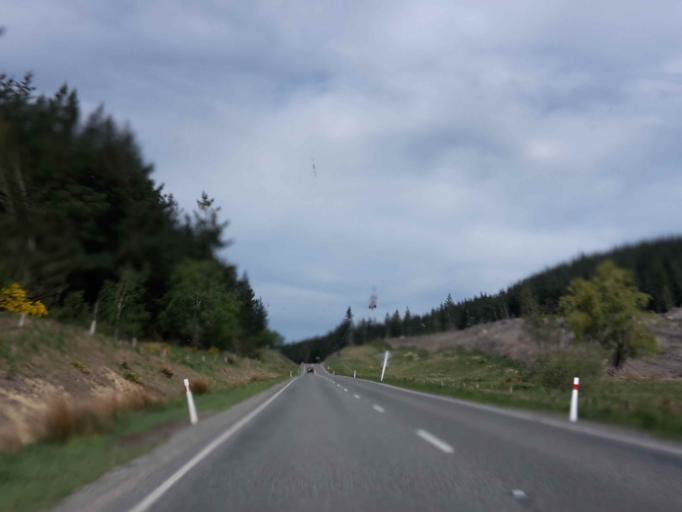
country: NZ
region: Canterbury
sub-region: Timaru District
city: Pleasant Point
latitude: -44.1217
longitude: 171.0689
